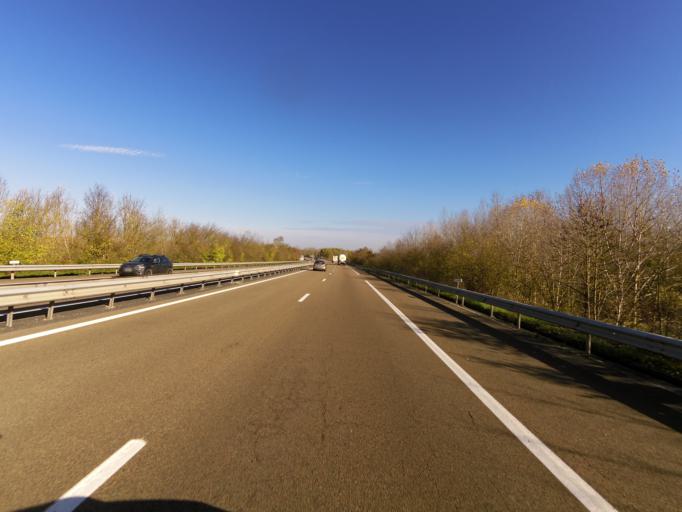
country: FR
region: Champagne-Ardenne
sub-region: Departement de la Marne
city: Fagnieres
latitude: 48.9837
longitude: 4.2916
